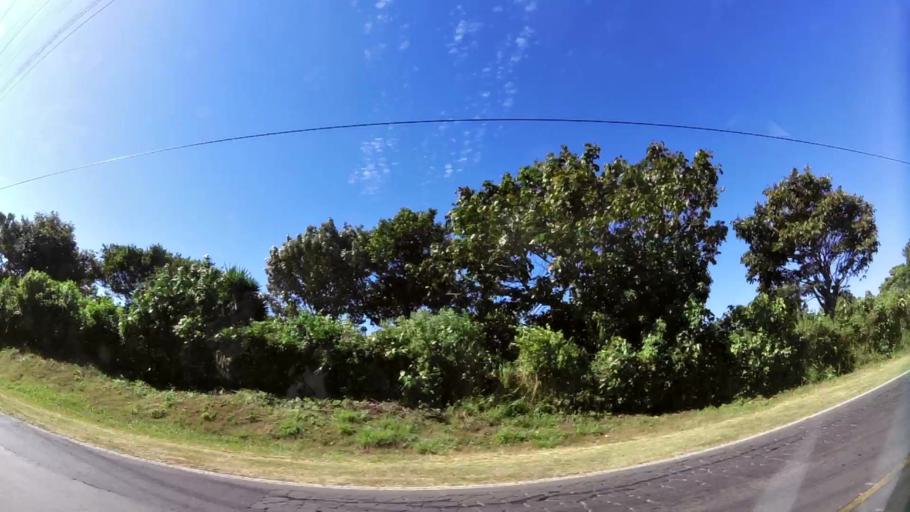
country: SV
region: Ahuachapan
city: Concepcion de Ataco
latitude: 13.8579
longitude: -89.8501
